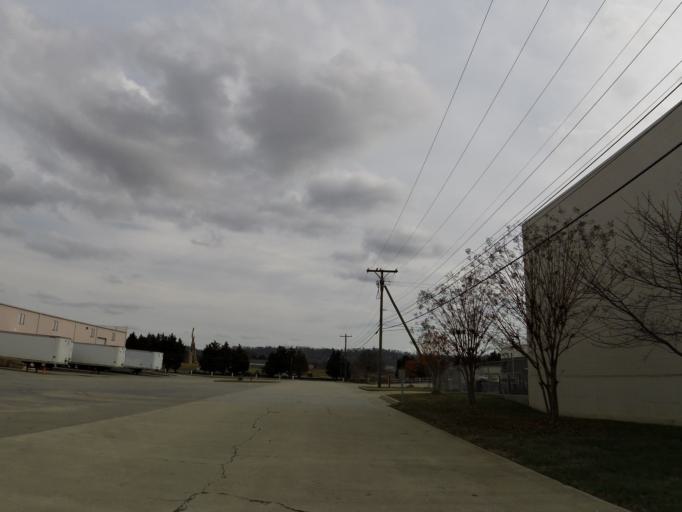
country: US
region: Tennessee
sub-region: Hamilton County
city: Chattanooga
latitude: 35.0271
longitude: -85.2971
